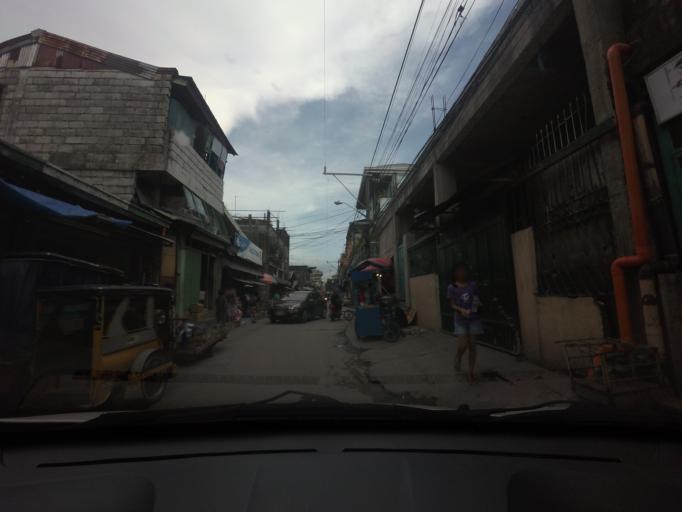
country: PH
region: Calabarzon
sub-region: Province of Rizal
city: Taguig
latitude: 14.4991
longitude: 121.0614
